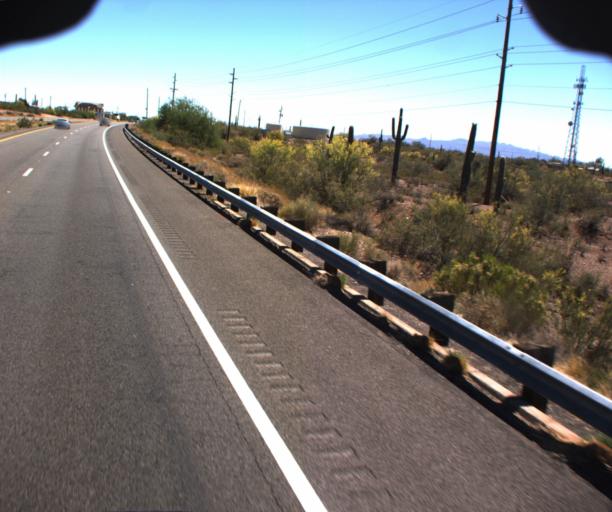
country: US
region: Arizona
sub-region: Maricopa County
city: Wickenburg
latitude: 33.8584
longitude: -112.6271
